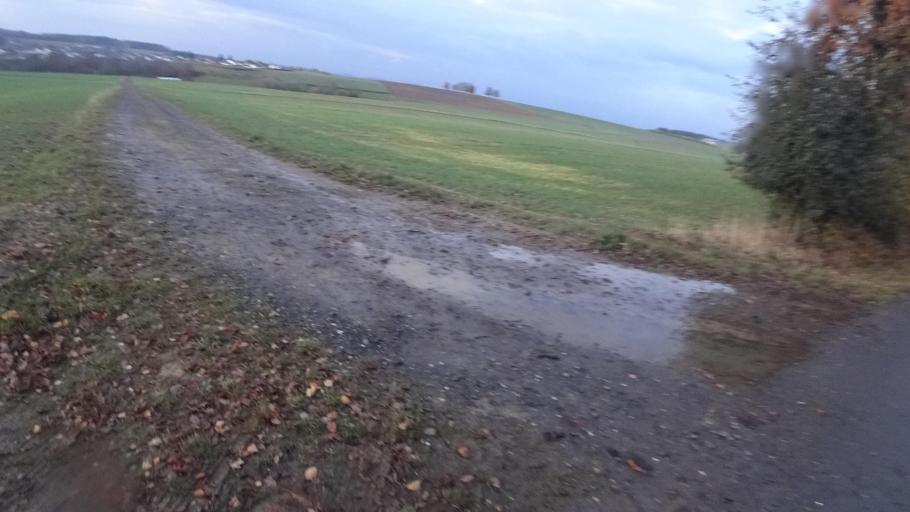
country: DE
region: Rheinland-Pfalz
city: Gondershausen
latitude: 50.1507
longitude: 7.5041
